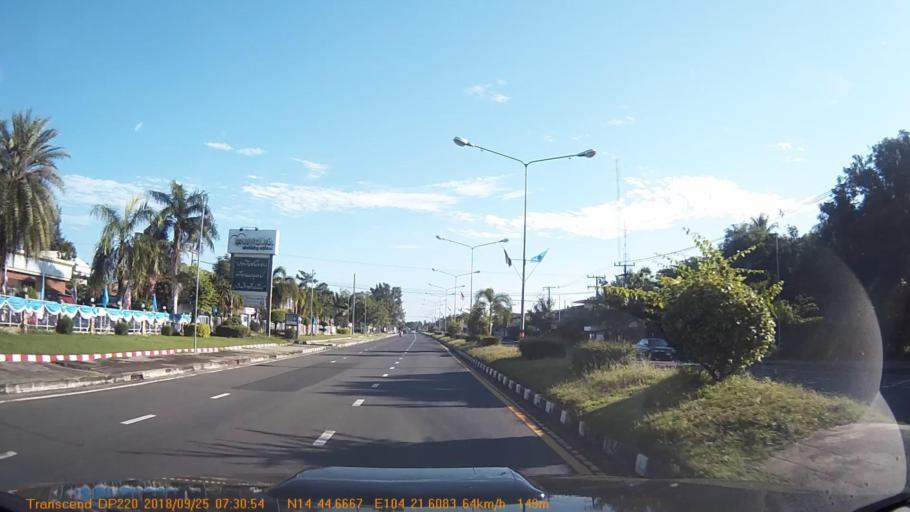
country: TH
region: Sisaket
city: Phrai Bueng
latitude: 14.7447
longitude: 104.3602
